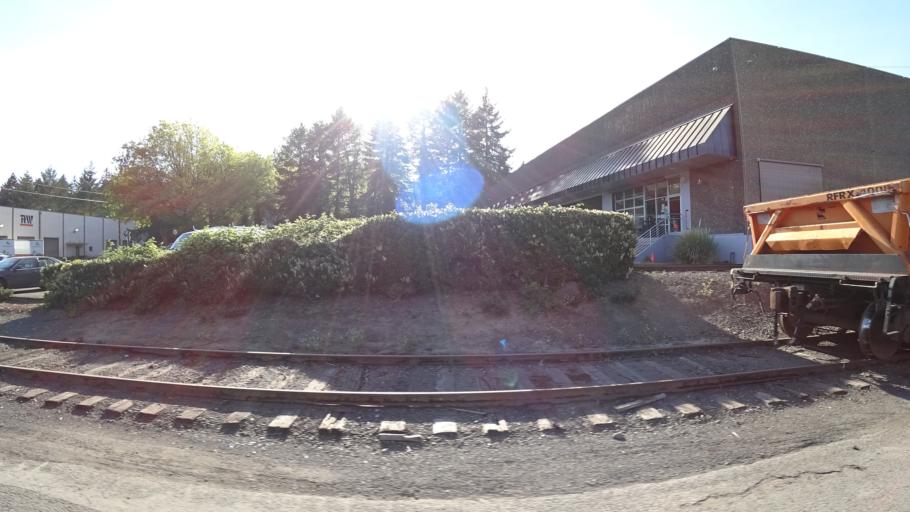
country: US
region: Oregon
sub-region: Clackamas County
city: Milwaukie
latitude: 45.4536
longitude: -122.6439
